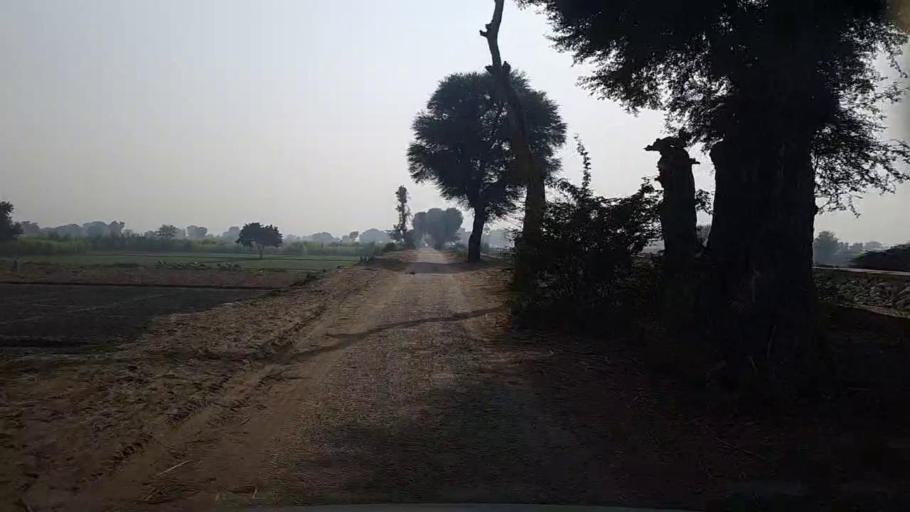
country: PK
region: Sindh
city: Setharja Old
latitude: 27.1174
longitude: 68.5099
